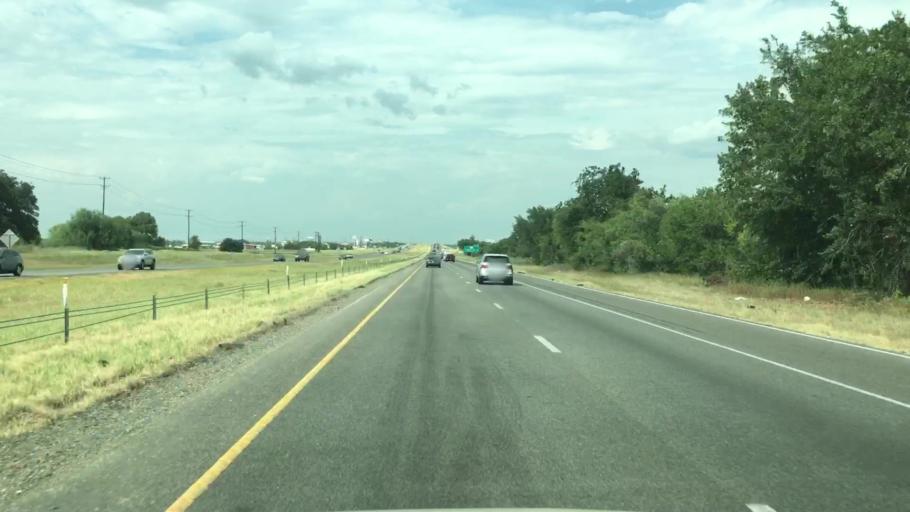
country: US
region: Texas
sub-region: Bexar County
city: Elmendorf
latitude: 29.2073
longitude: -98.4168
